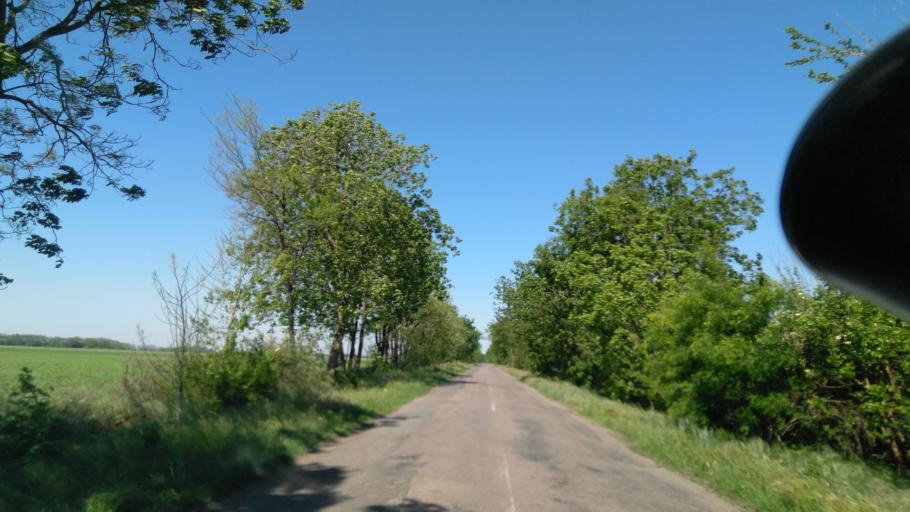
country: HU
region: Bekes
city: Kunagota
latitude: 46.4239
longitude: 21.1055
